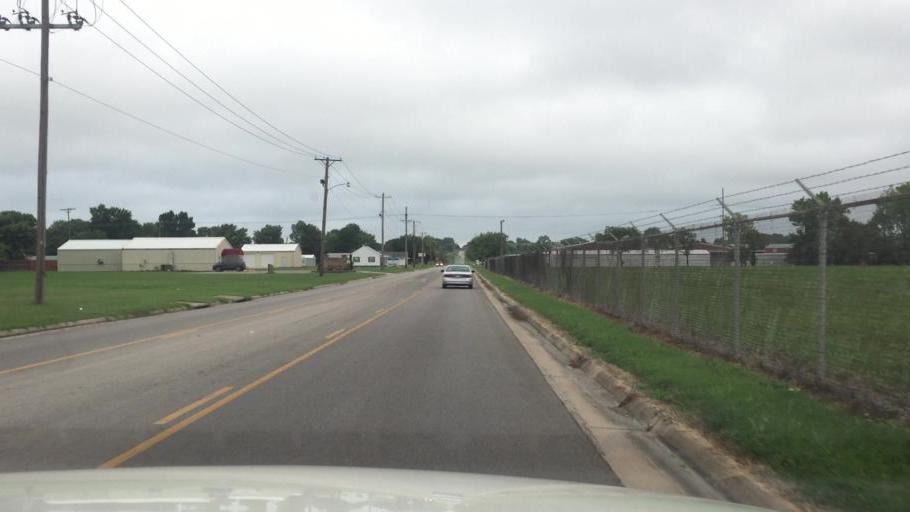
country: US
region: Kansas
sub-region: Montgomery County
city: Coffeyville
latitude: 37.0454
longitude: -95.6473
